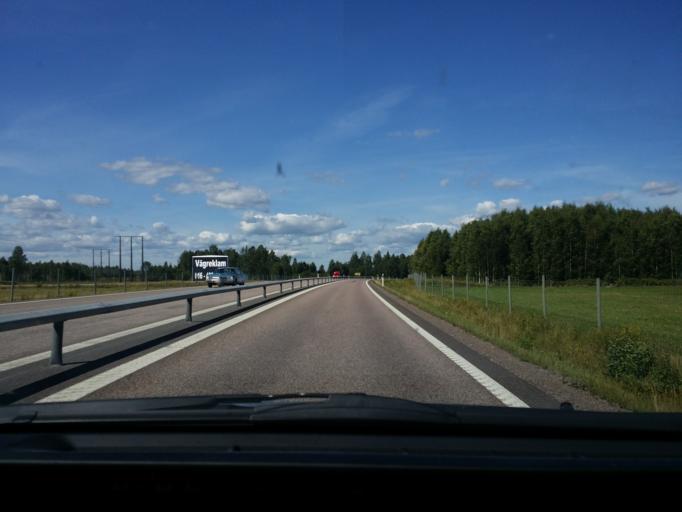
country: SE
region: Dalarna
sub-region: Hedemora Kommun
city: Brunna
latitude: 60.2500
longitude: 16.0184
